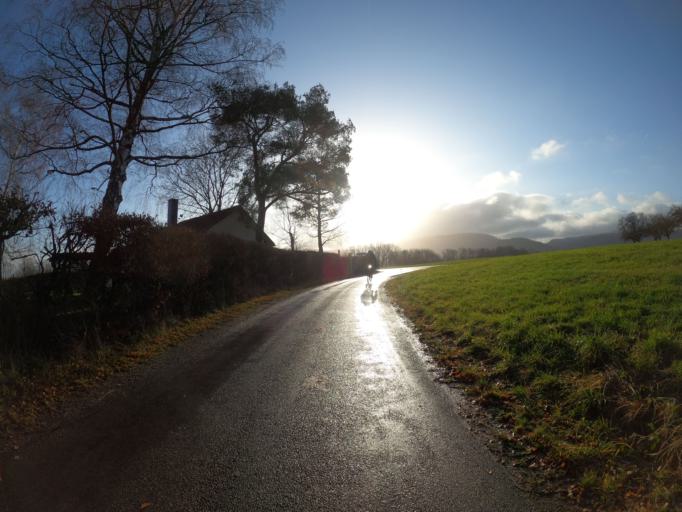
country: DE
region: Baden-Wuerttemberg
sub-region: Regierungsbezirk Stuttgart
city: Boll
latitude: 48.6516
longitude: 9.6214
